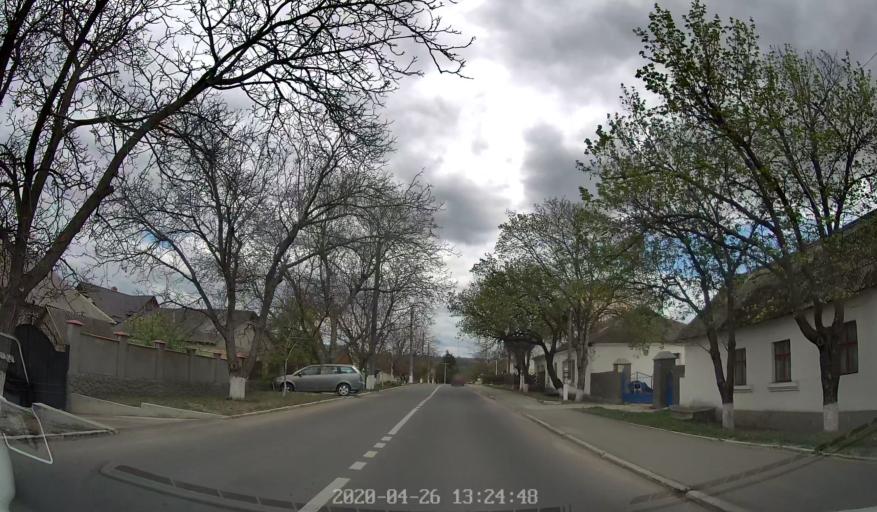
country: MD
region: Criuleni
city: Criuleni
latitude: 47.2068
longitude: 29.1645
